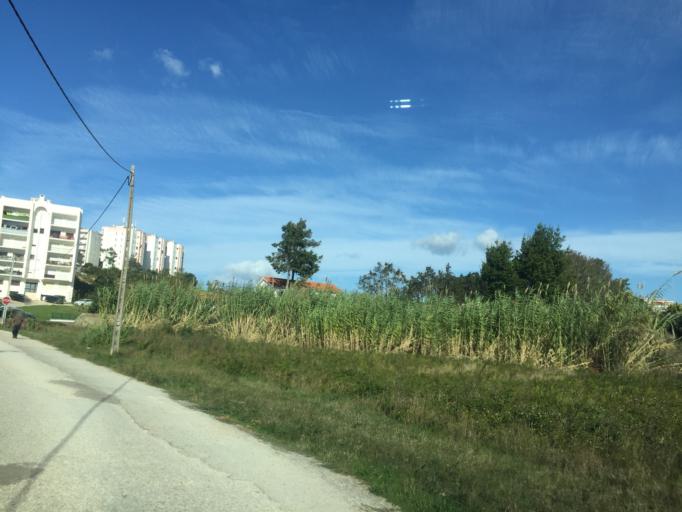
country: PT
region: Coimbra
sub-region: Figueira da Foz
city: Tavarede
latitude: 40.1652
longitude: -8.8425
